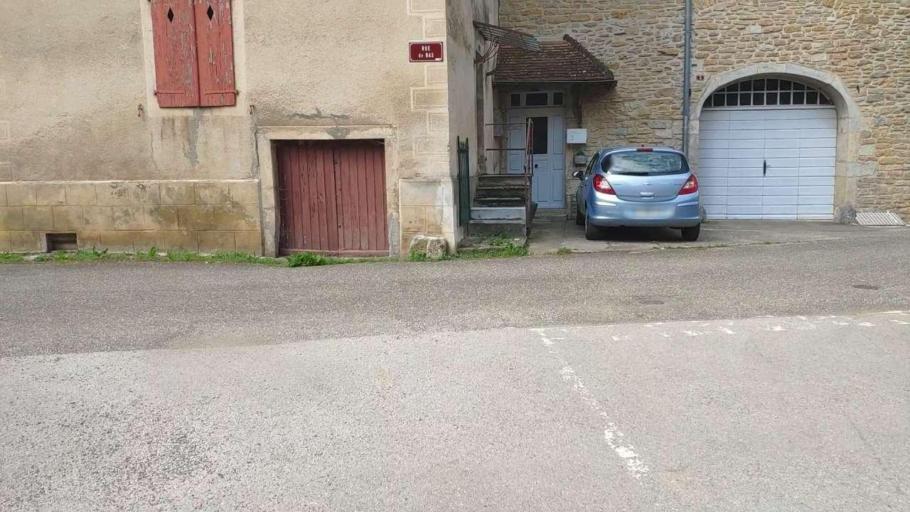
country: FR
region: Franche-Comte
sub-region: Departement du Jura
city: Perrigny
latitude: 46.7686
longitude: 5.6200
